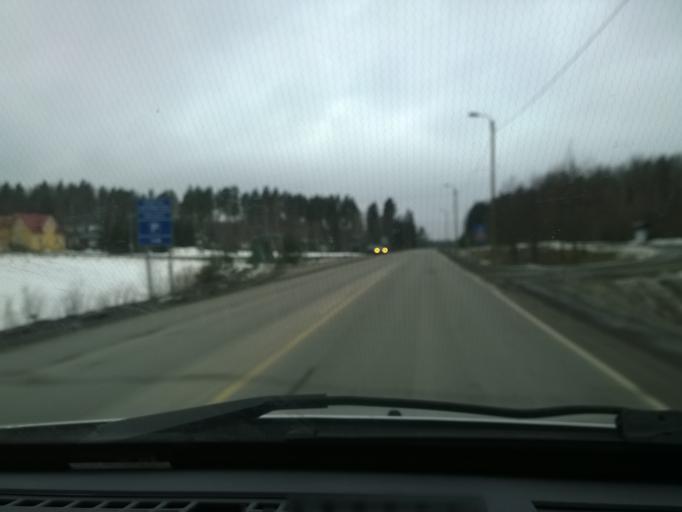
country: FI
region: Pirkanmaa
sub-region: Tampere
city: Lempaeaelae
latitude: 61.2953
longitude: 23.6995
